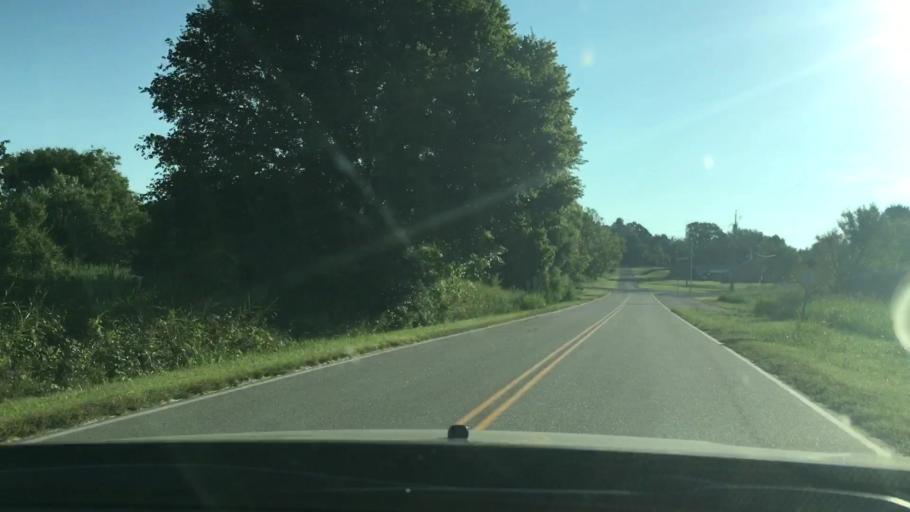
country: US
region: Oklahoma
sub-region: Pontotoc County
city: Ada
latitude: 34.7000
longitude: -96.4338
